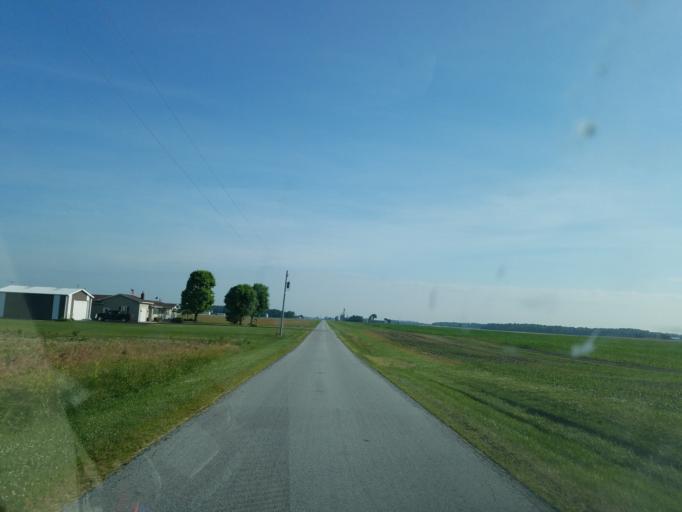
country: US
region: Ohio
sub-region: Hardin County
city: Kenton
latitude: 40.7383
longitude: -83.6716
